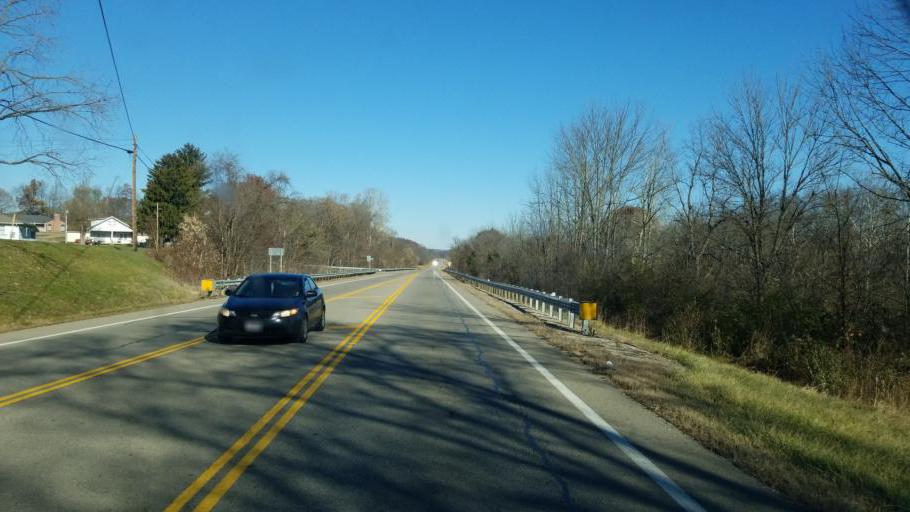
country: US
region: Ohio
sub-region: Coshocton County
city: Coshocton
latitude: 40.1940
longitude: -81.8949
